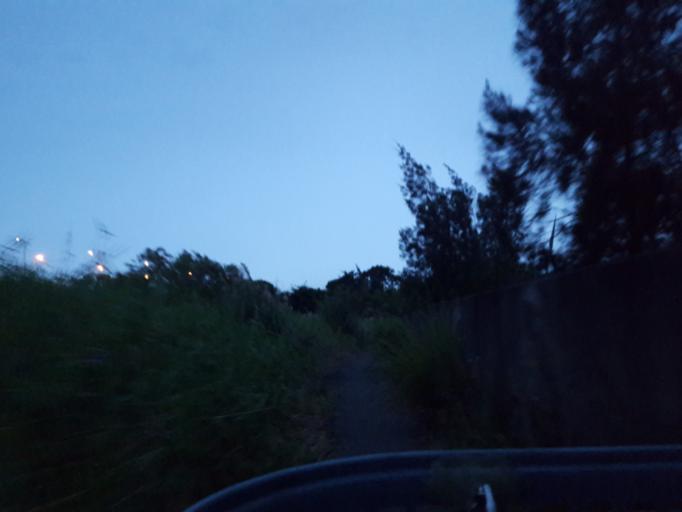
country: TW
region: Taiwan
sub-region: Hsinchu
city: Hsinchu
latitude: 24.7410
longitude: 120.9027
